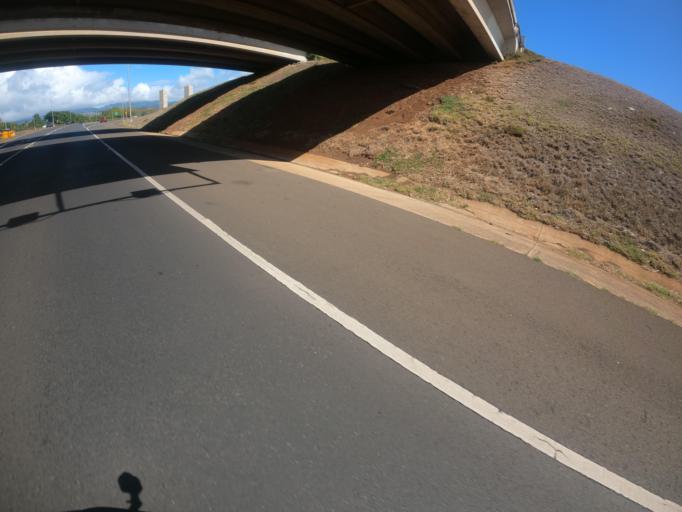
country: US
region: Hawaii
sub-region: Honolulu County
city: Pearl City, Manana
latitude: 21.3938
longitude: -157.9894
